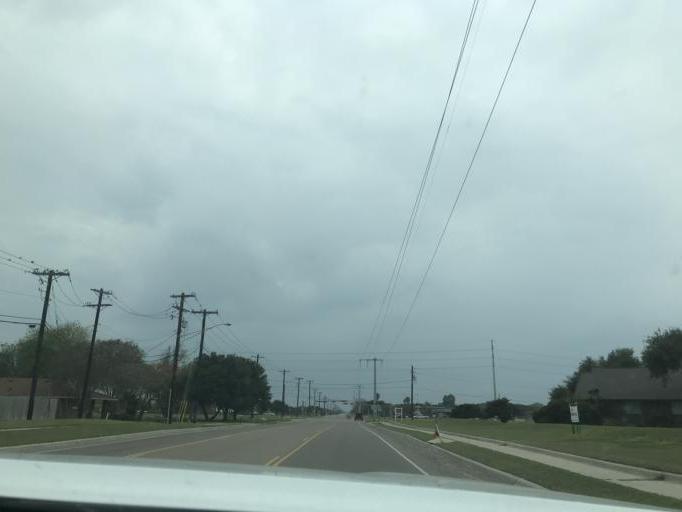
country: US
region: Texas
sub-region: Nueces County
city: Corpus Christi
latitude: 27.6766
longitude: -97.3491
